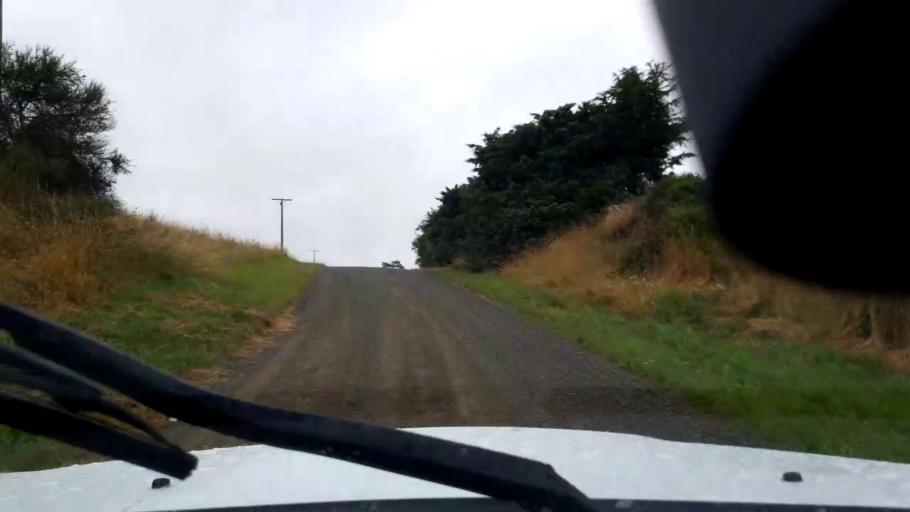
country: NZ
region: Canterbury
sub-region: Timaru District
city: Pleasant Point
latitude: -44.2532
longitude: 171.2187
